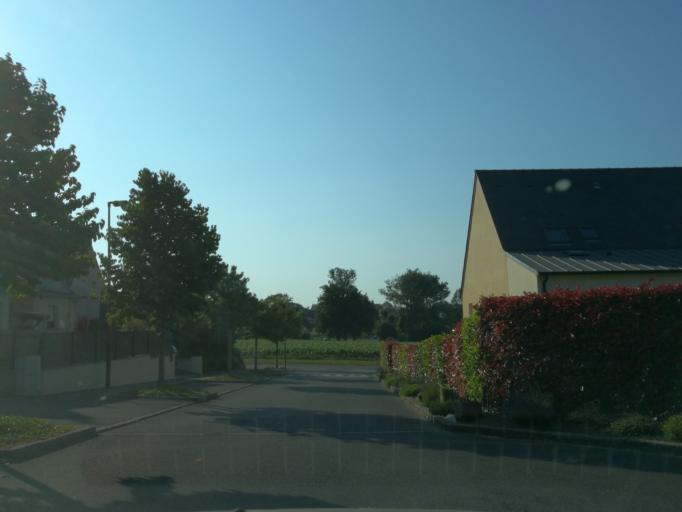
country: FR
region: Brittany
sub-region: Departement d'Ille-et-Vilaine
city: Bedee
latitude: 48.1761
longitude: -1.9485
